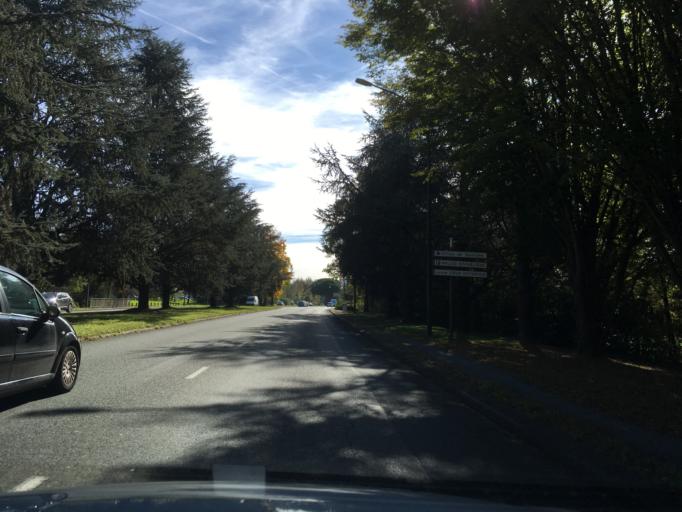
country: FR
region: Aquitaine
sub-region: Departement des Pyrenees-Atlantiques
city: Pau
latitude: 43.3266
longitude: -0.3569
